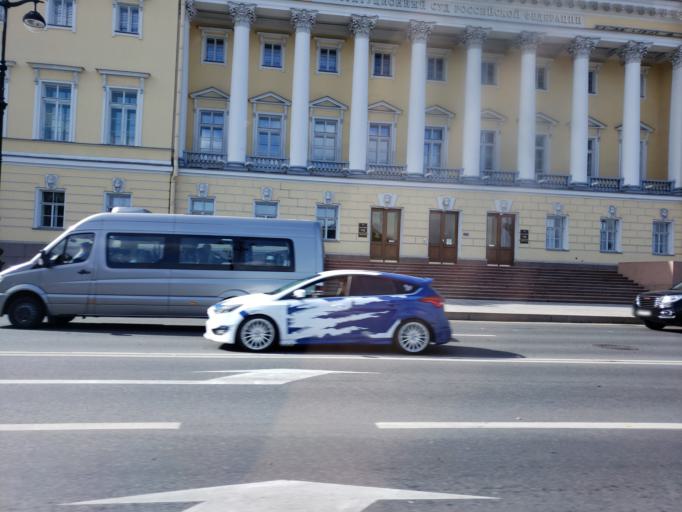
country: RU
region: St.-Petersburg
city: Saint Petersburg
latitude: 59.9360
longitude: 30.3016
